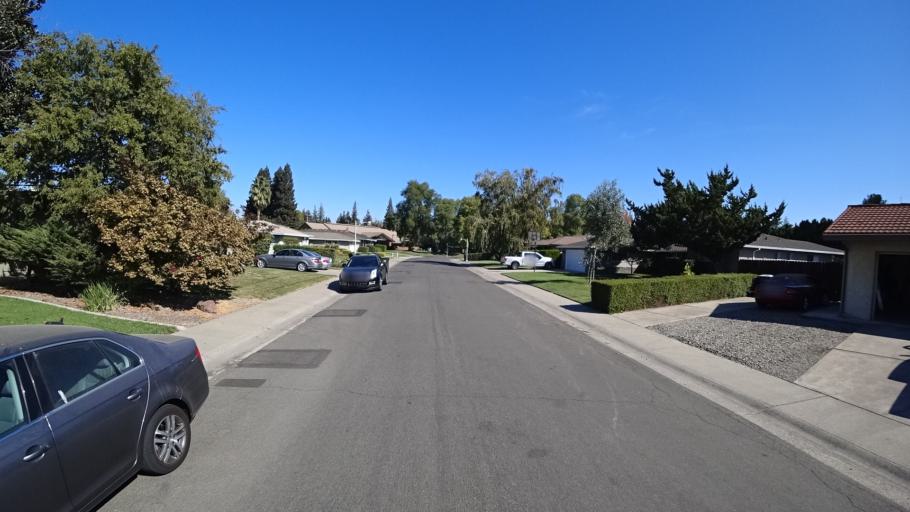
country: US
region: California
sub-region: Sacramento County
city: Parkway
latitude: 38.4992
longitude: -121.5195
